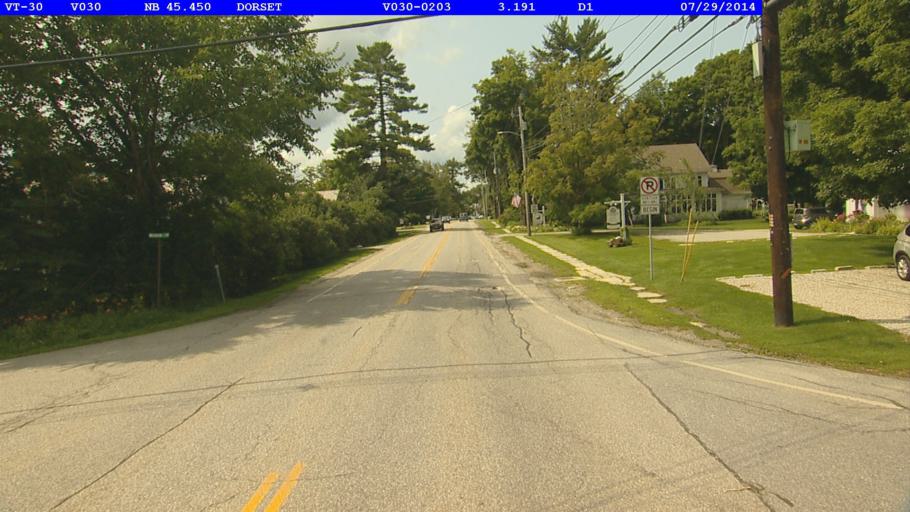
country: US
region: Vermont
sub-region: Bennington County
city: Manchester Center
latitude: 43.2529
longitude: -73.0965
